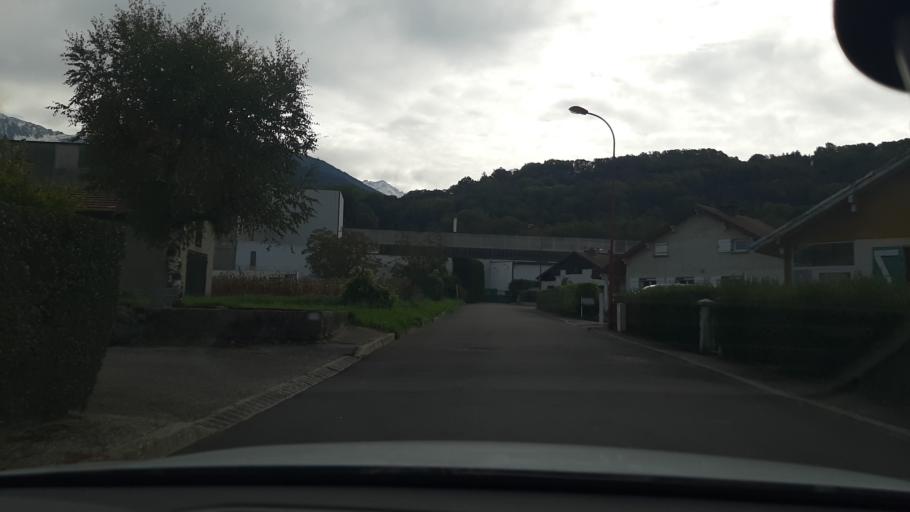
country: FR
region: Rhone-Alpes
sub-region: Departement de la Savoie
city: La Rochette
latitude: 45.4529
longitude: 6.1142
